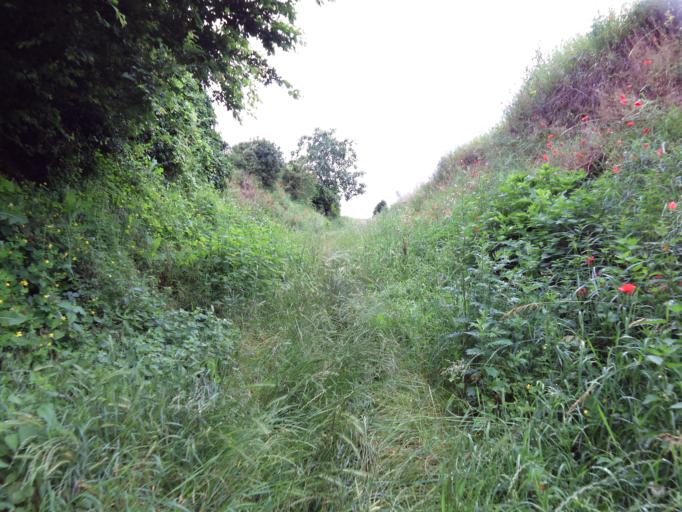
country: DE
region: Rheinland-Pfalz
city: Dirmstein
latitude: 49.5697
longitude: 8.2394
